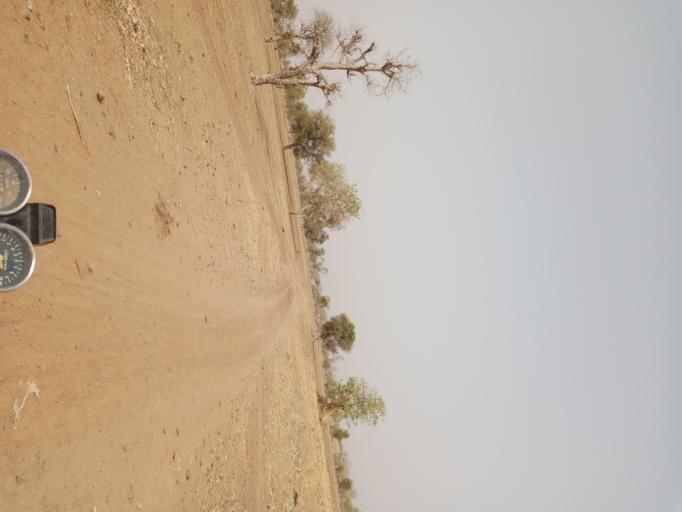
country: BF
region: Est
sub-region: Gnagna Province
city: Bogande
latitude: 13.2786
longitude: -0.1425
